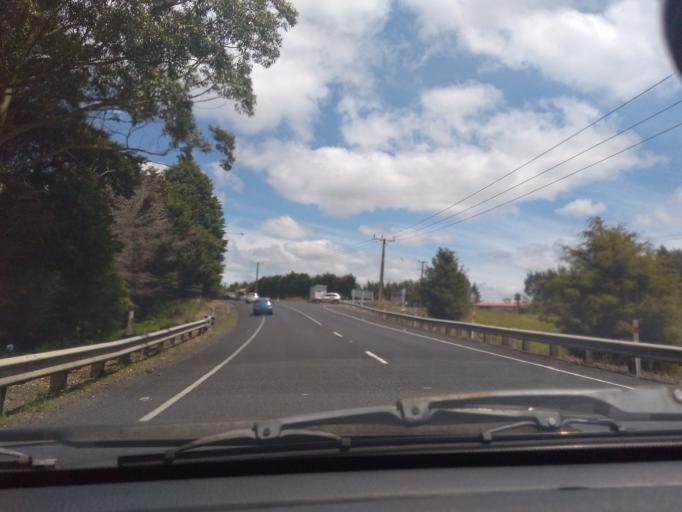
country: NZ
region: Northland
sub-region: Far North District
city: Kerikeri
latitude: -35.1888
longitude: 173.9104
